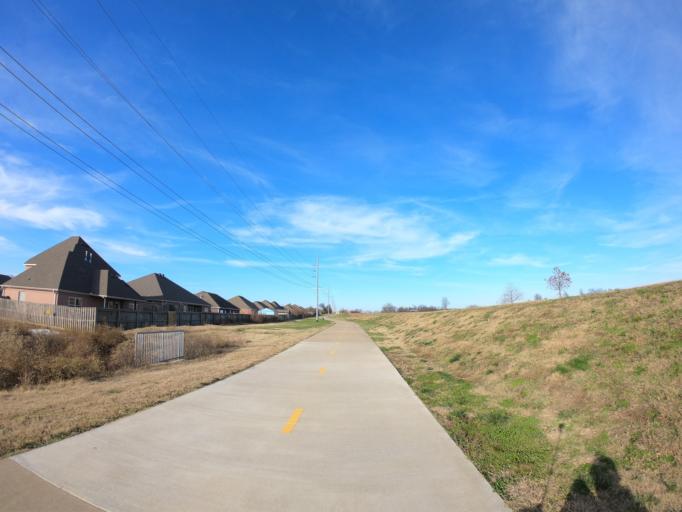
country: US
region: Arkansas
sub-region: Benton County
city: Lowell
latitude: 36.2702
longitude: -94.1676
